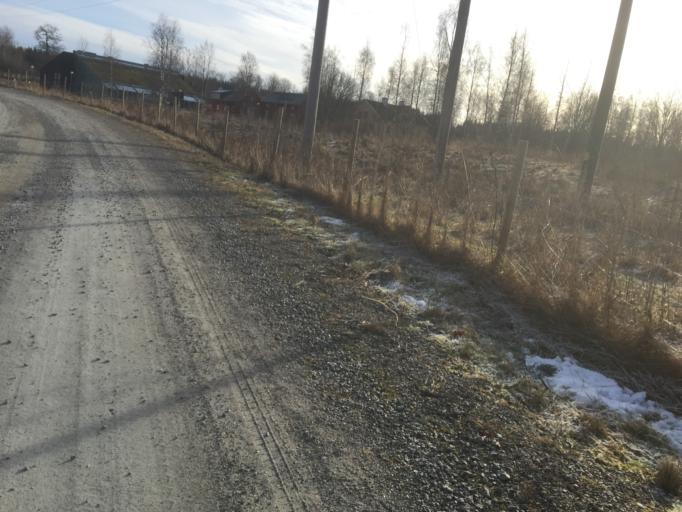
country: SE
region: Joenkoeping
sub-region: Aneby Kommun
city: Aneby
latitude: 57.8222
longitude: 14.8169
